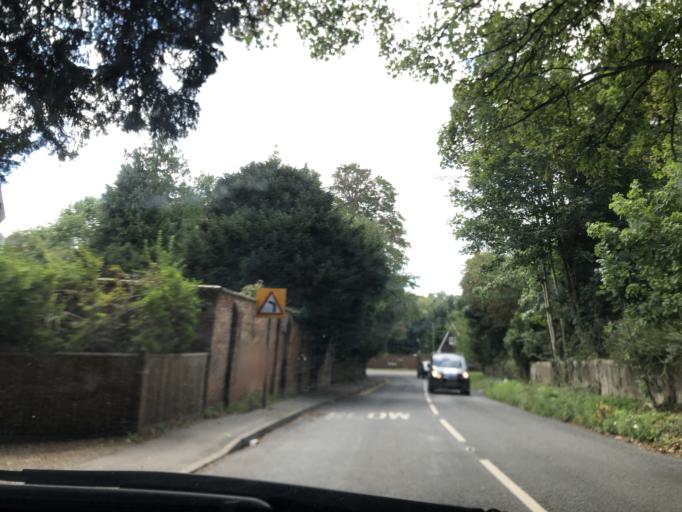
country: GB
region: England
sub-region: Kent
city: Halstead
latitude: 51.2800
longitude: 0.1270
